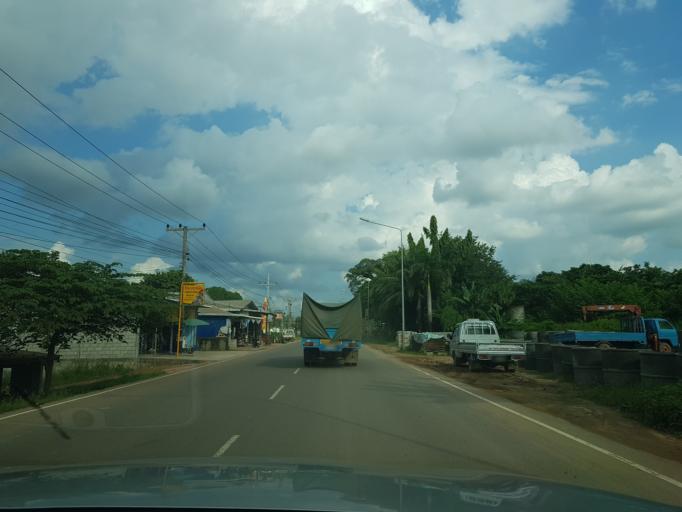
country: TH
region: Nong Khai
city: Si Chiang Mai
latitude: 17.9750
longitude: 102.5013
